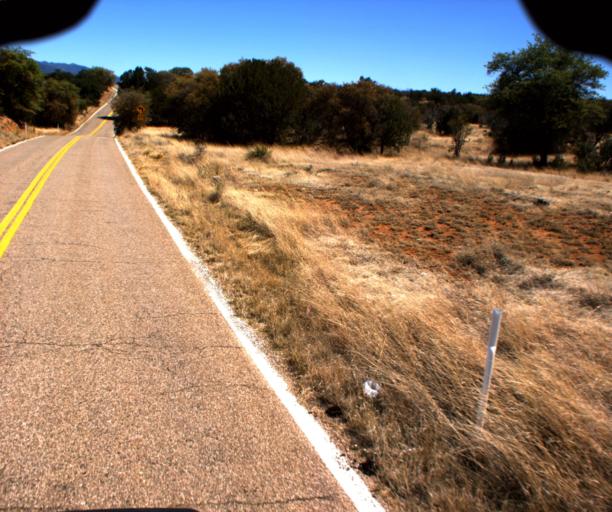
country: US
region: Arizona
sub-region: Cochise County
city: Huachuca City
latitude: 31.5531
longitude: -110.5490
